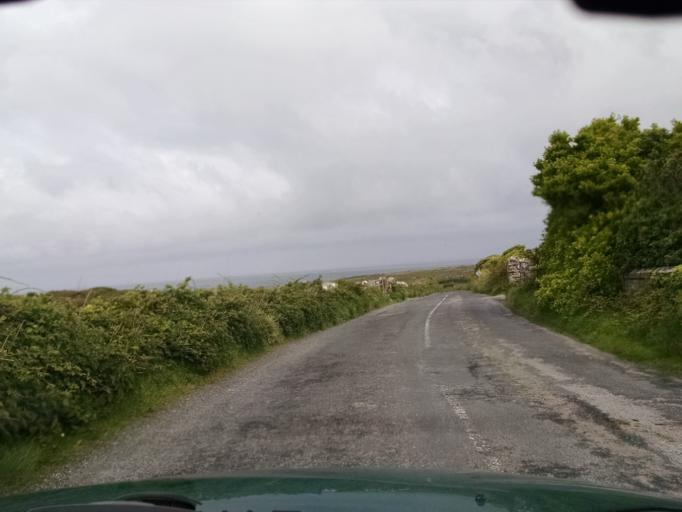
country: IE
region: Connaught
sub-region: County Galway
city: Bearna
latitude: 53.0517
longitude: -9.3463
